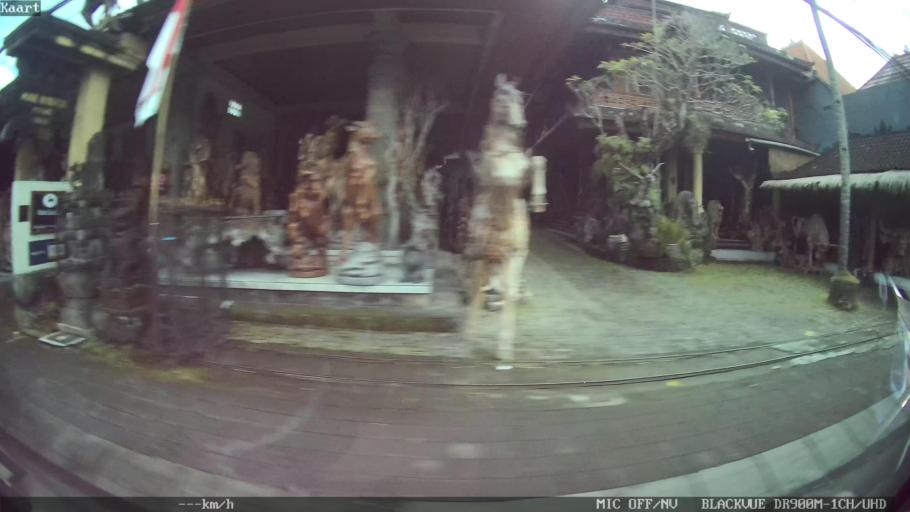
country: ID
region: Bali
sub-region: Kabupaten Gianyar
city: Ubud
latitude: -8.5241
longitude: 115.2724
